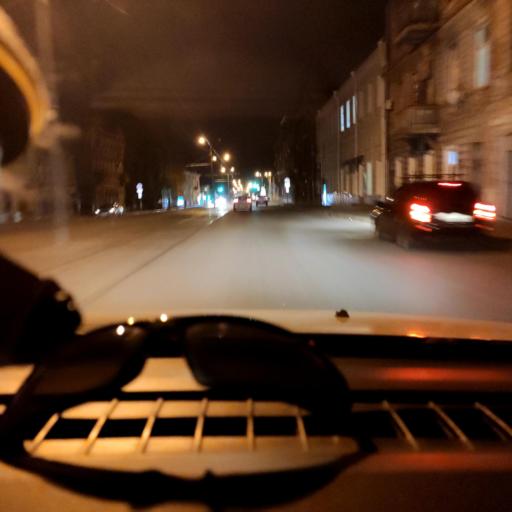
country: RU
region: Samara
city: Rozhdestveno
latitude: 53.1843
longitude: 50.0893
